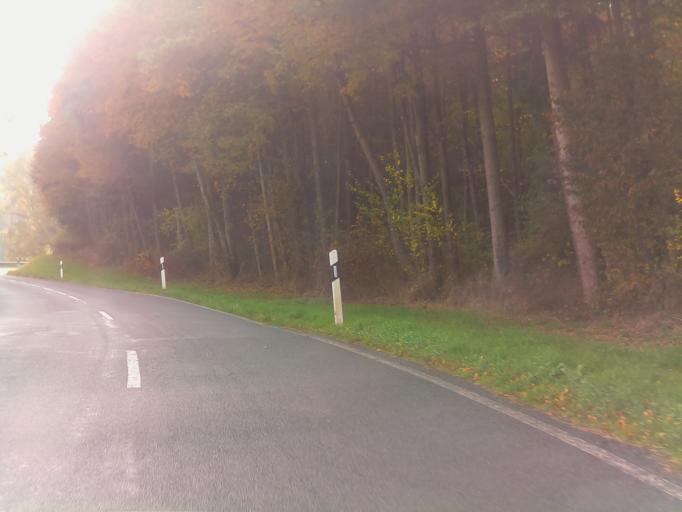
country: DE
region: Baden-Wuerttemberg
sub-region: Regierungsbezirk Stuttgart
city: Krautheim
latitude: 49.3986
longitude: 9.5722
